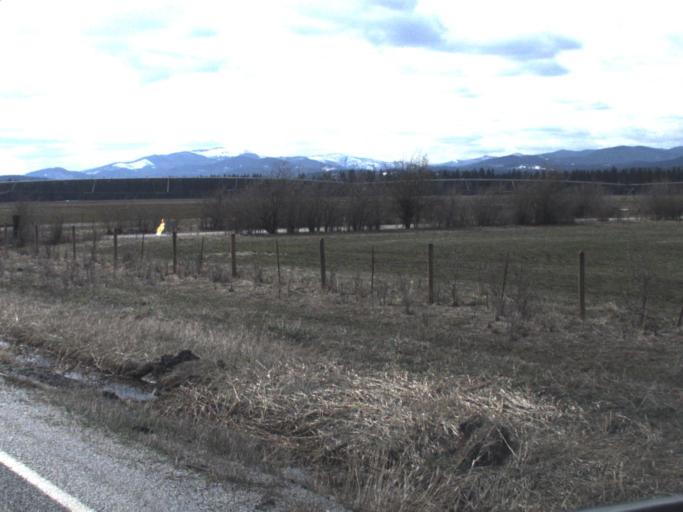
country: US
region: Washington
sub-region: Pend Oreille County
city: Newport
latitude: 48.3571
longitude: -117.3046
